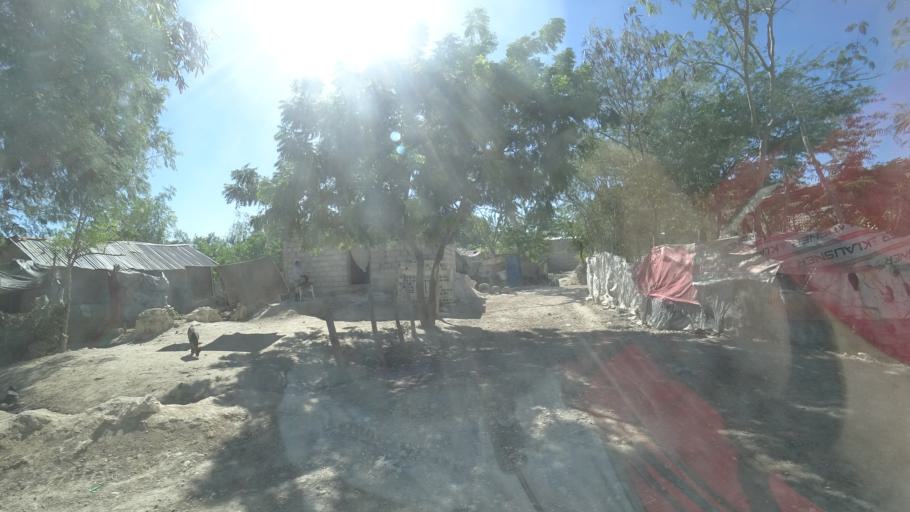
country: HT
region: Ouest
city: Croix des Bouquets
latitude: 18.6520
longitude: -72.2584
